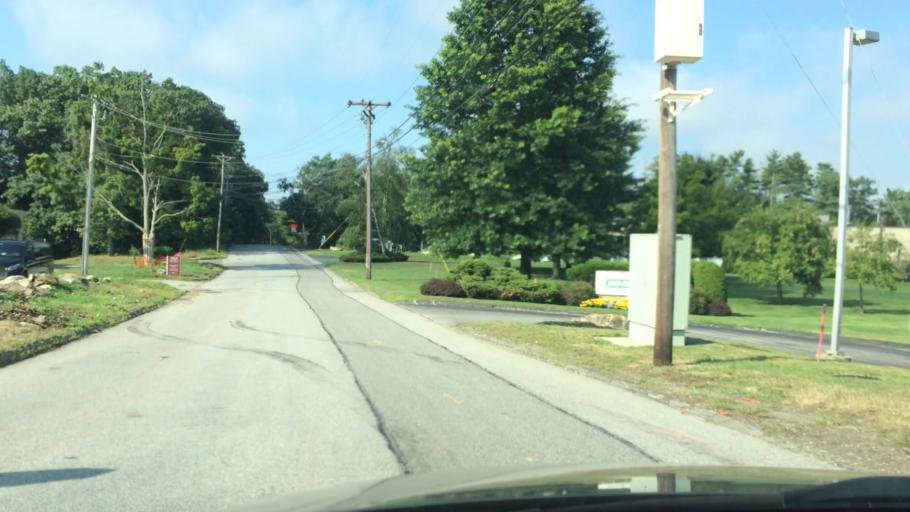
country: US
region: Massachusetts
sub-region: Middlesex County
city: Billerica
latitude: 42.5309
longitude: -71.2606
